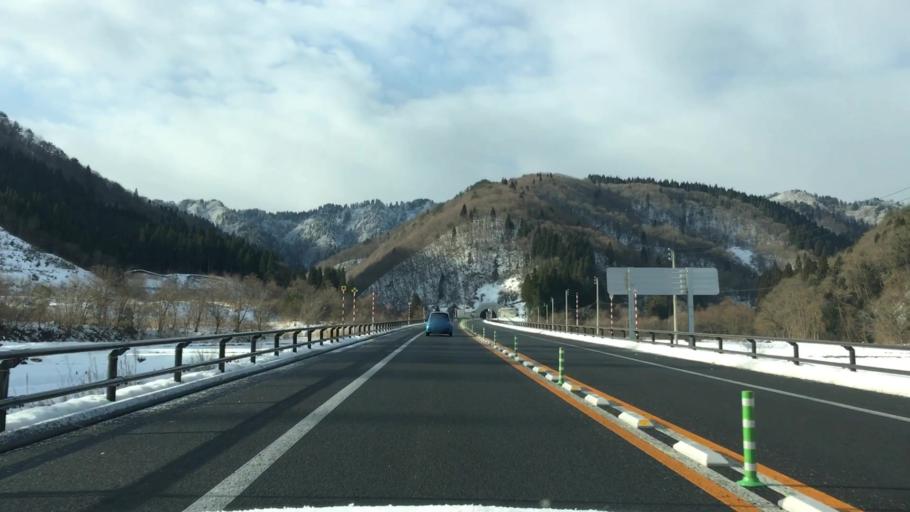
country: JP
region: Akita
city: Odate
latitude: 40.2328
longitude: 140.4942
